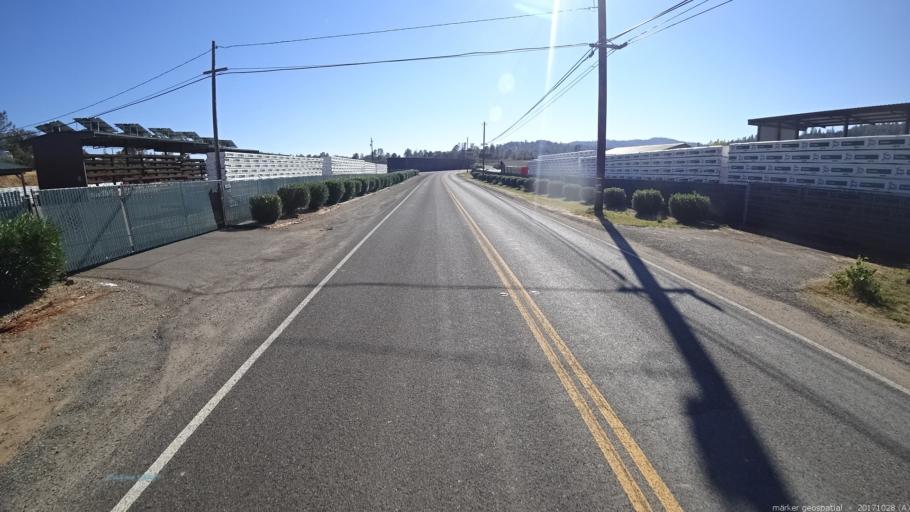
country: US
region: California
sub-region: Shasta County
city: Shasta
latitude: 40.6058
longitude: -122.4625
